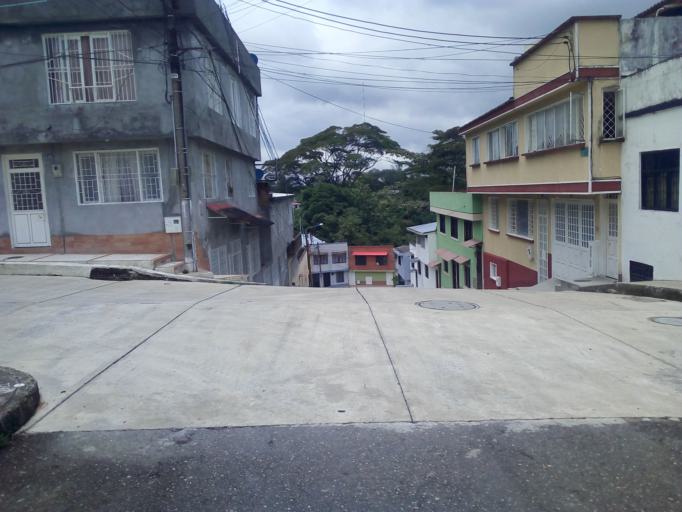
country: CO
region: Tolima
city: Ibague
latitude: 4.4521
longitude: -75.2417
